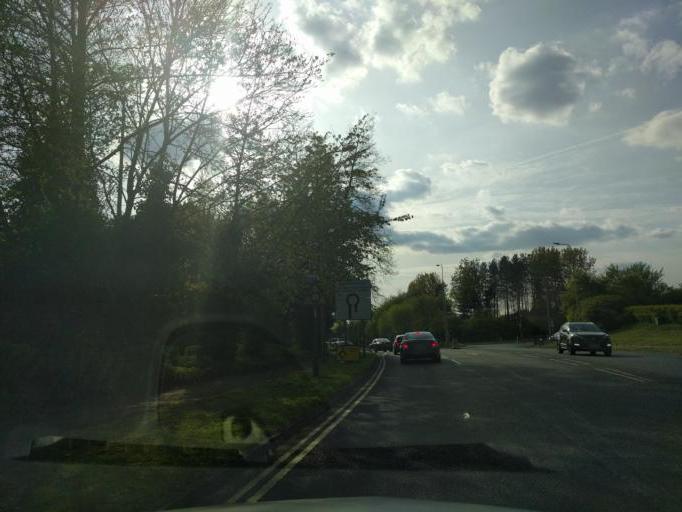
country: GB
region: England
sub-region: Suffolk
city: Bury St Edmunds
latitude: 52.2400
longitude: 0.7357
